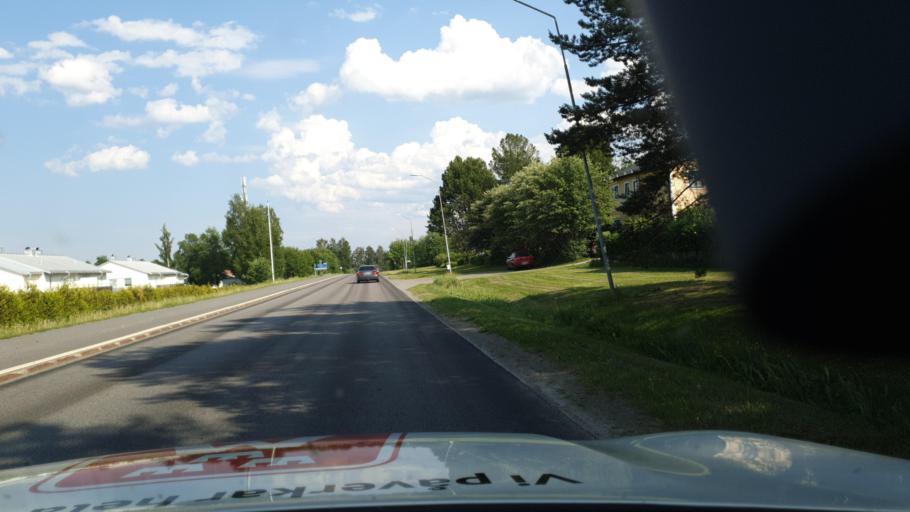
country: SE
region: Vaesterbotten
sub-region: Skelleftea Kommun
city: Viken
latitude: 64.7469
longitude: 20.9163
